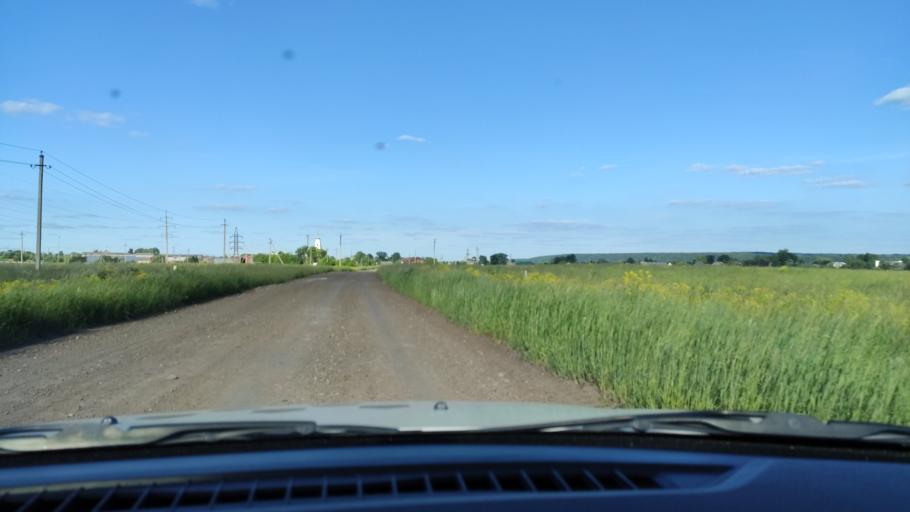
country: RU
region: Perm
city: Orda
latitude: 57.3035
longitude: 56.6410
